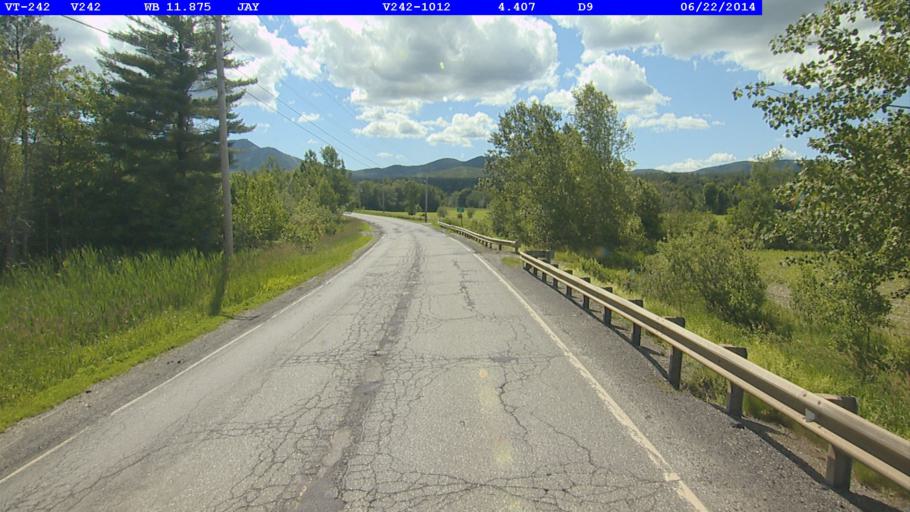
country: US
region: Vermont
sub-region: Orleans County
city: Newport
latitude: 44.9493
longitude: -72.4315
